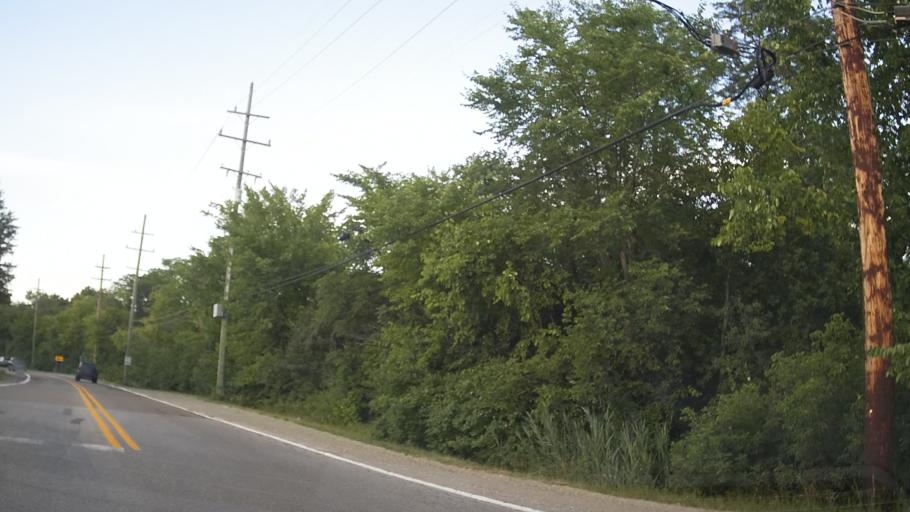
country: US
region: Michigan
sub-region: Macomb County
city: Clinton
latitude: 42.5965
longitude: -82.9166
